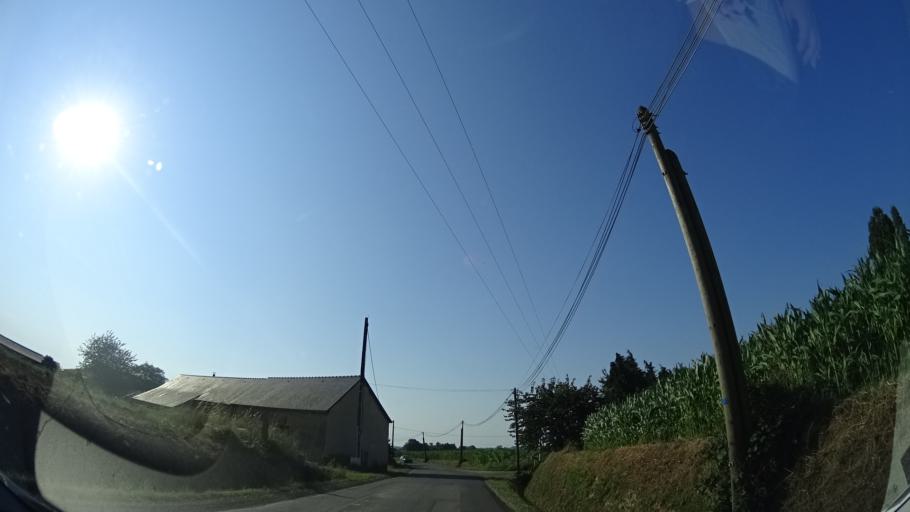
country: FR
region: Brittany
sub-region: Departement d'Ille-et-Vilaine
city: Pace
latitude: 48.1779
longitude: -1.7943
